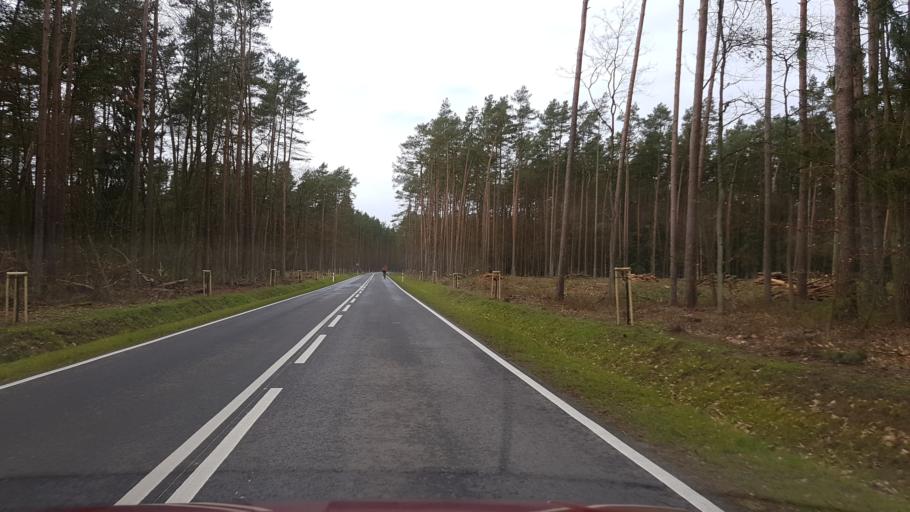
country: PL
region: West Pomeranian Voivodeship
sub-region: Powiat policki
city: Police
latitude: 53.6562
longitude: 14.4760
